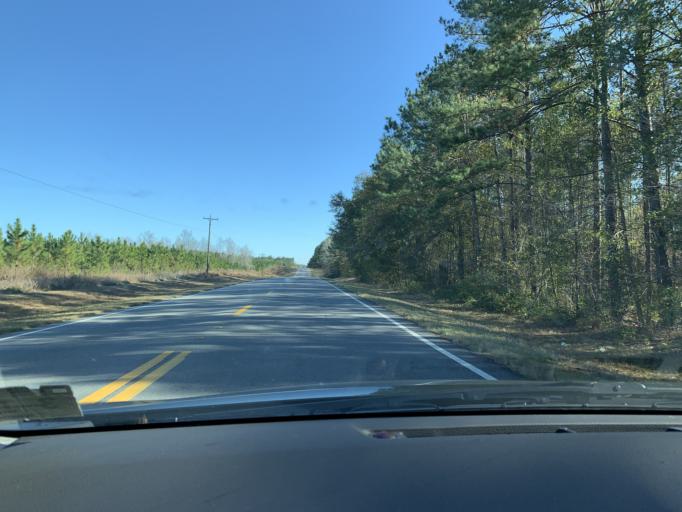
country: US
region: Georgia
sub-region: Ben Hill County
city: Fitzgerald
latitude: 31.7608
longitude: -83.1176
